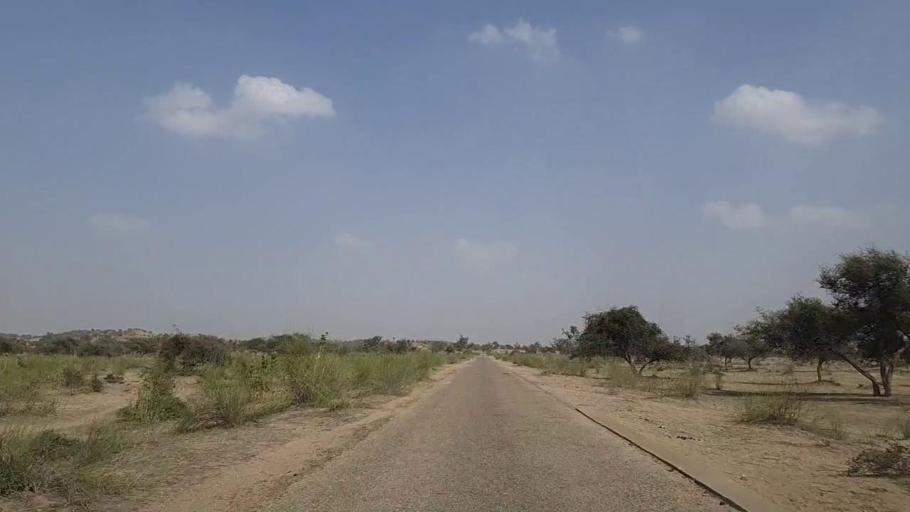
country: PK
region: Sindh
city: Islamkot
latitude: 24.7996
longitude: 70.1227
